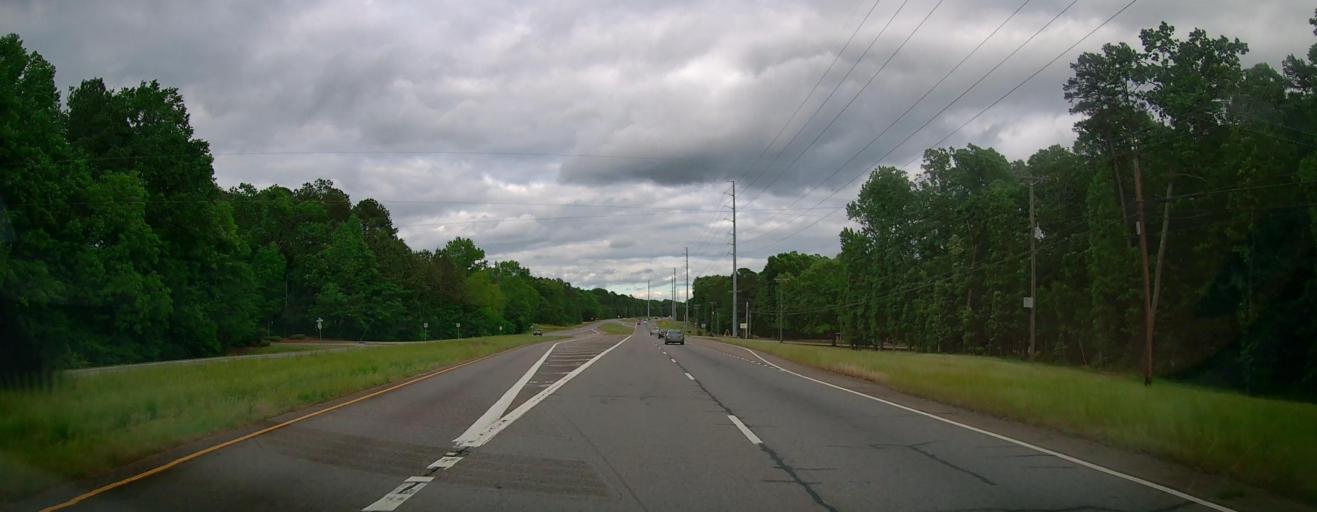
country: US
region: Georgia
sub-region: Oconee County
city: Bogart
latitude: 33.9184
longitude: -83.5409
